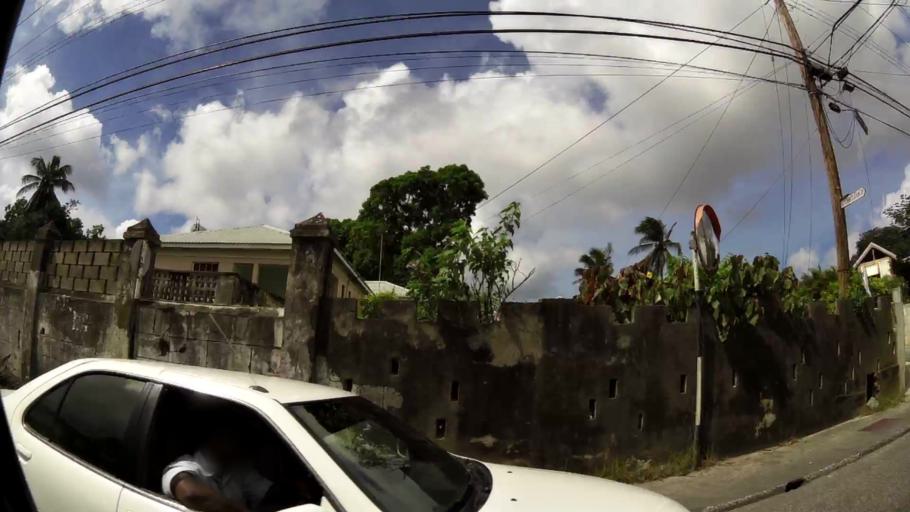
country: BB
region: Saint Michael
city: Bridgetown
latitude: 13.1193
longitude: -59.6127
